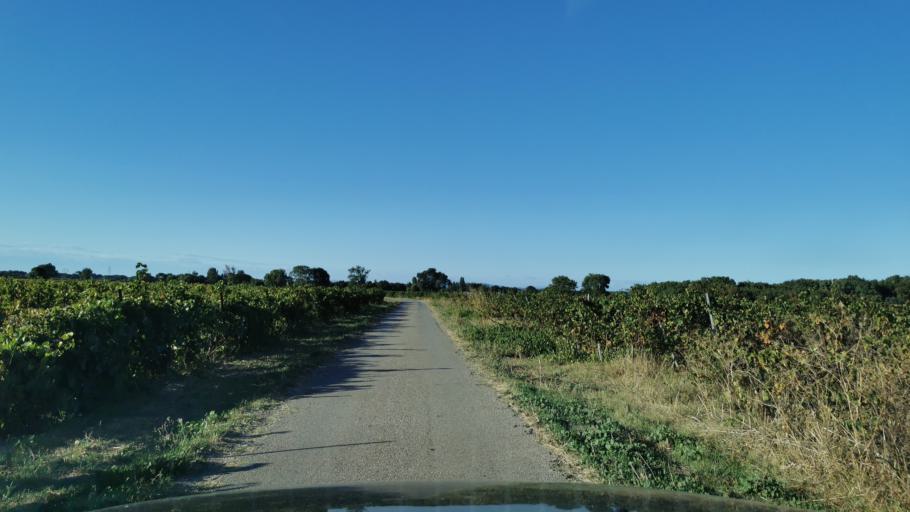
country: FR
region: Languedoc-Roussillon
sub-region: Departement de l'Aude
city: Coursan
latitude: 43.2560
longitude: 3.0211
